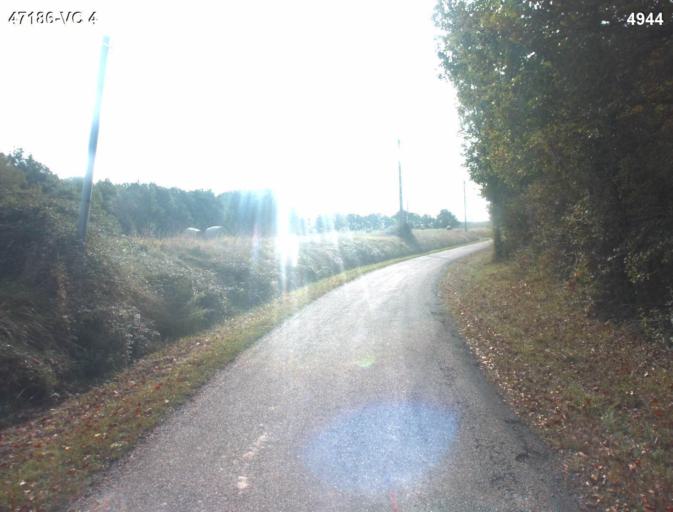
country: FR
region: Aquitaine
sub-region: Departement du Lot-et-Garonne
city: Sainte-Colombe-en-Bruilhois
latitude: 44.1913
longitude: 0.4566
